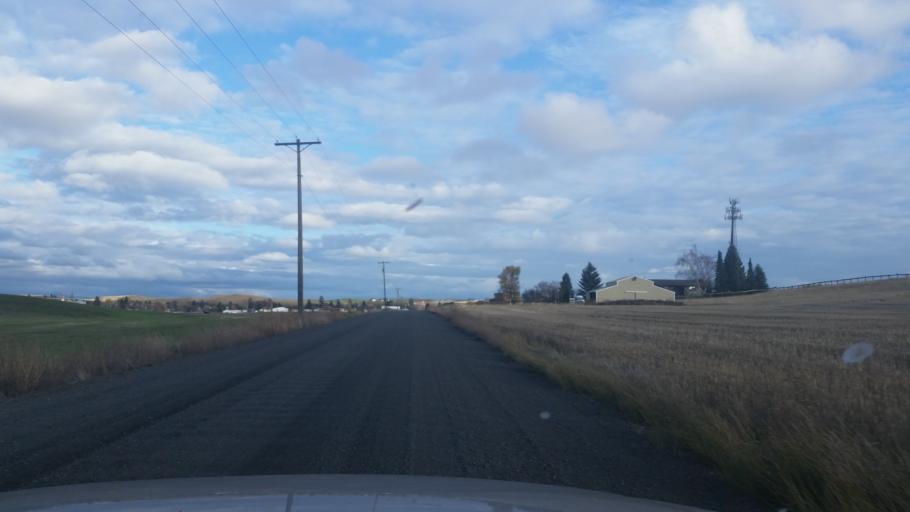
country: US
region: Washington
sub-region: Spokane County
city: Cheney
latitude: 47.4274
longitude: -117.3954
